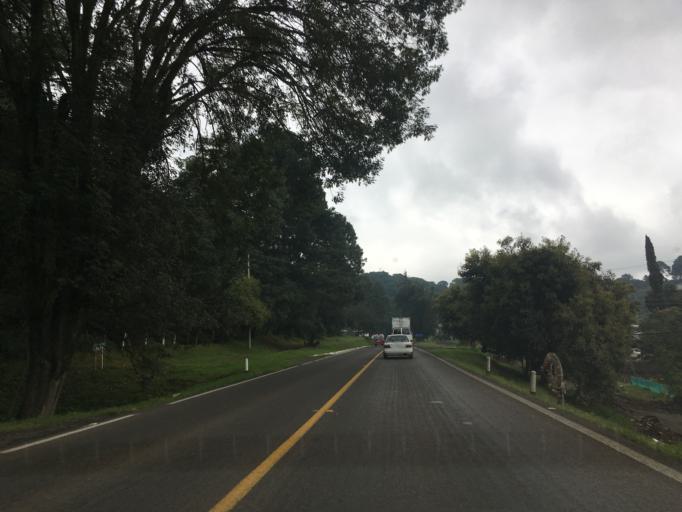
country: MX
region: Michoacan
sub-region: Uruapan
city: Toreo Bajo (El Toreo Bajo)
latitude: 19.4500
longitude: -102.0065
